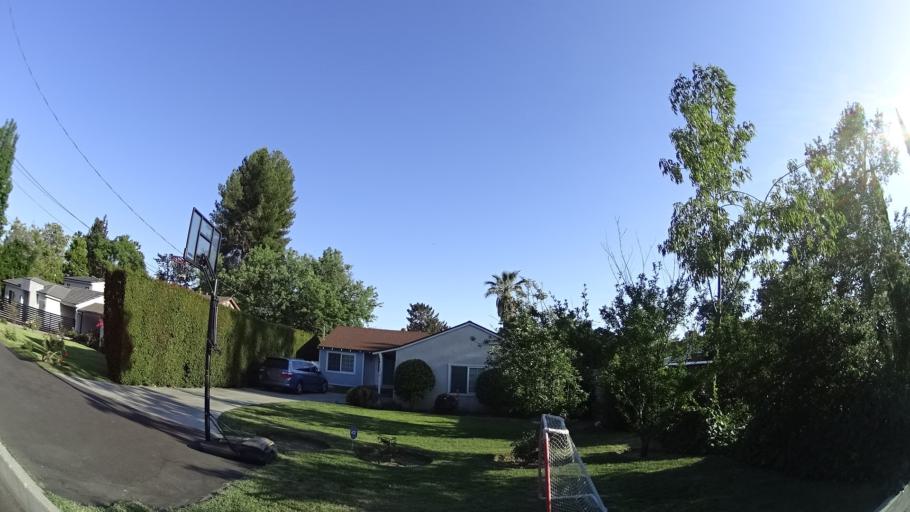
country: US
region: California
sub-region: Los Angeles County
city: North Hollywood
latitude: 34.1640
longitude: -118.4036
